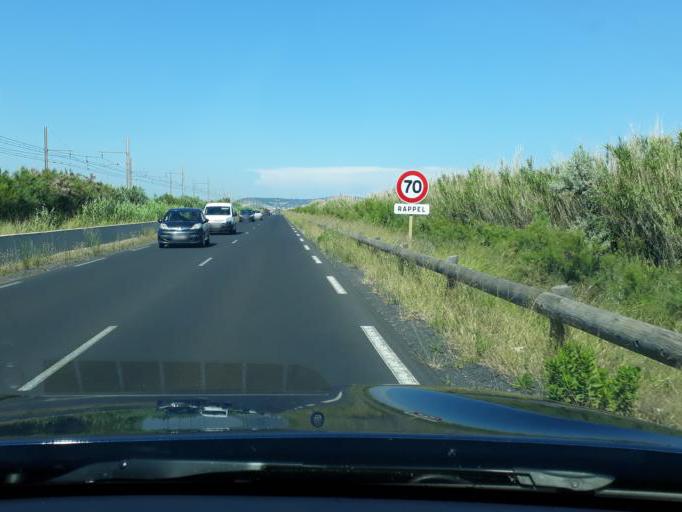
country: FR
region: Languedoc-Roussillon
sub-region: Departement de l'Herault
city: Meze
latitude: 43.3602
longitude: 3.6036
